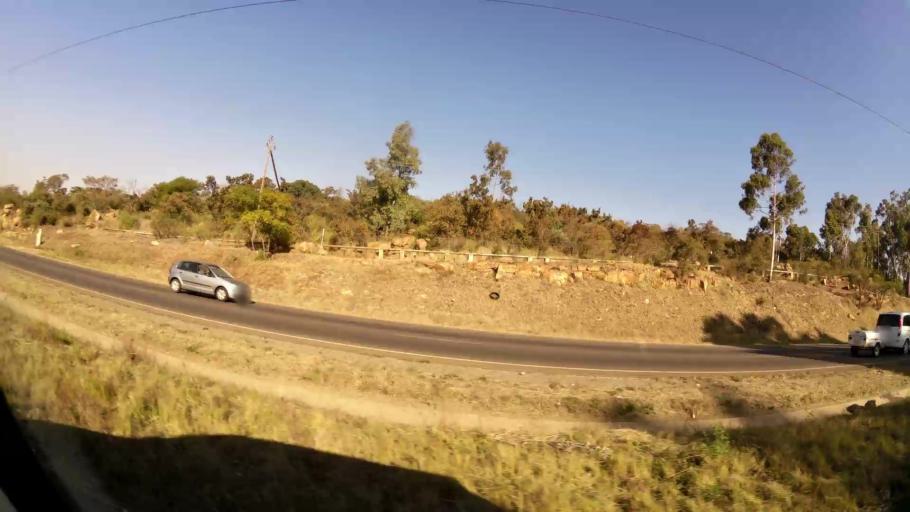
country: ZA
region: Gauteng
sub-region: City of Tshwane Metropolitan Municipality
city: Pretoria
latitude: -25.7820
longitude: 28.3348
